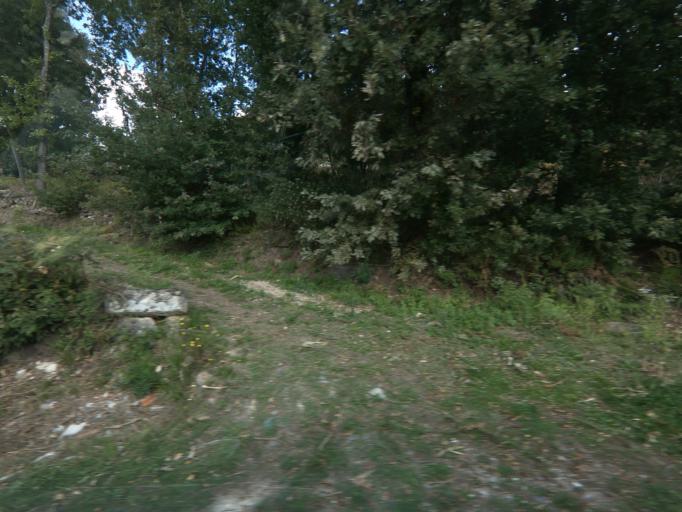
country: PT
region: Vila Real
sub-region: Vila Real
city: Vila Real
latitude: 41.3283
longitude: -7.7703
